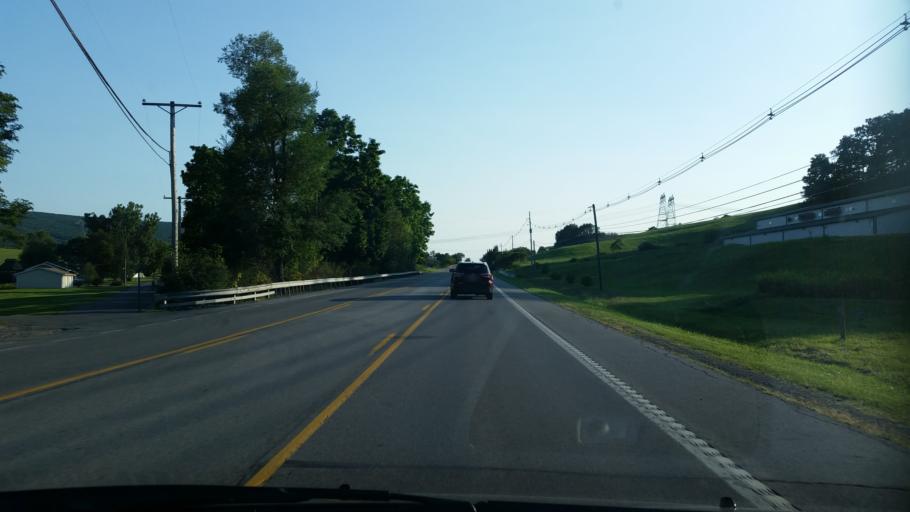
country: US
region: Pennsylvania
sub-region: Blair County
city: Bellwood
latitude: 40.5816
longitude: -78.3279
